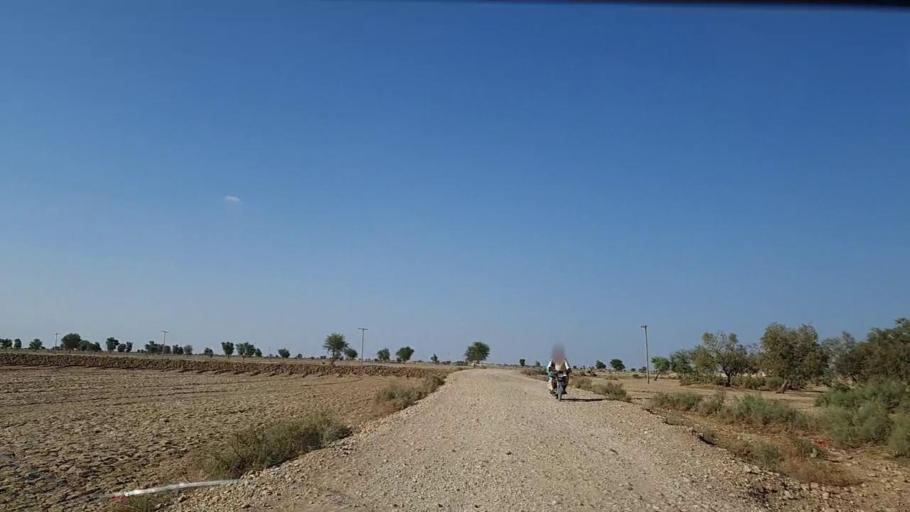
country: PK
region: Sindh
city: Johi
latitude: 26.5298
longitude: 67.5297
